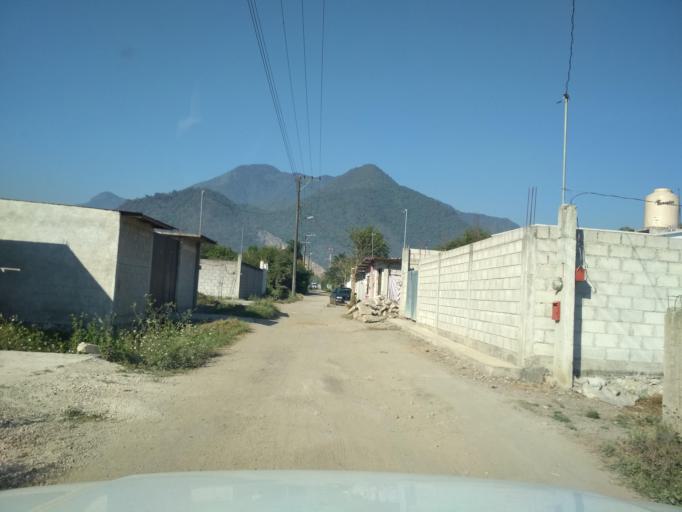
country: MX
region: Veracruz
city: Jalapilla
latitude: 18.8258
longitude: -97.0769
